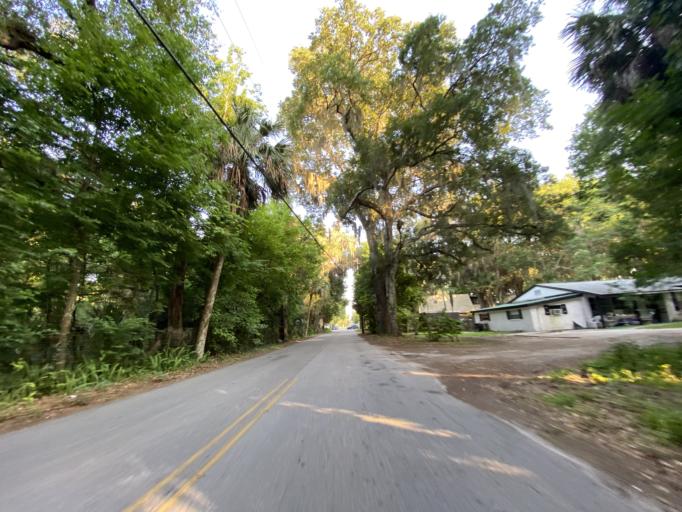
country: US
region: Florida
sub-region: Volusia County
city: Port Orange
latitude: 29.1395
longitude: -81.0093
